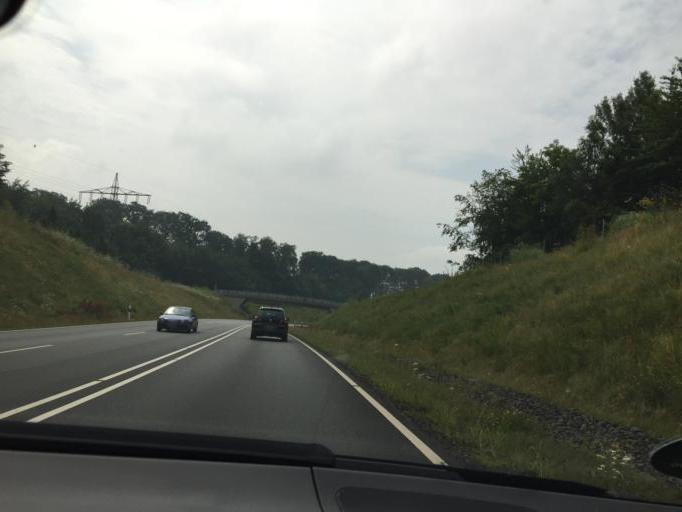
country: DE
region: Rheinland-Pfalz
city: Rengsdorf
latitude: 50.5072
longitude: 7.4808
